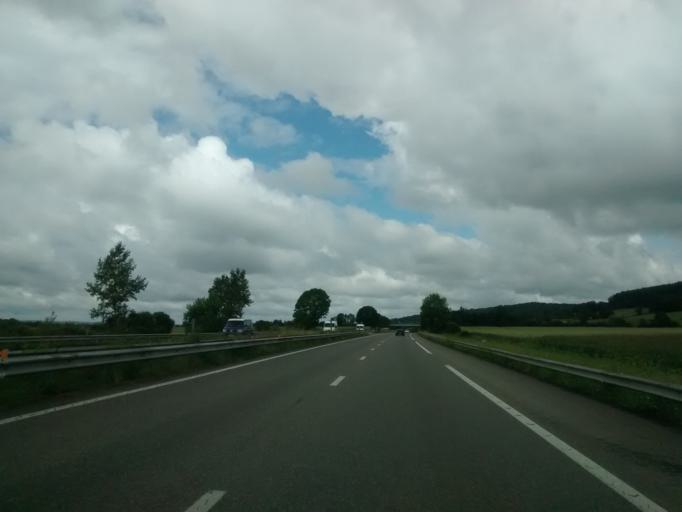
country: FR
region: Aquitaine
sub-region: Departement des Pyrenees-Atlantiques
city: Denguin
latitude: 43.3751
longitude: -0.4927
